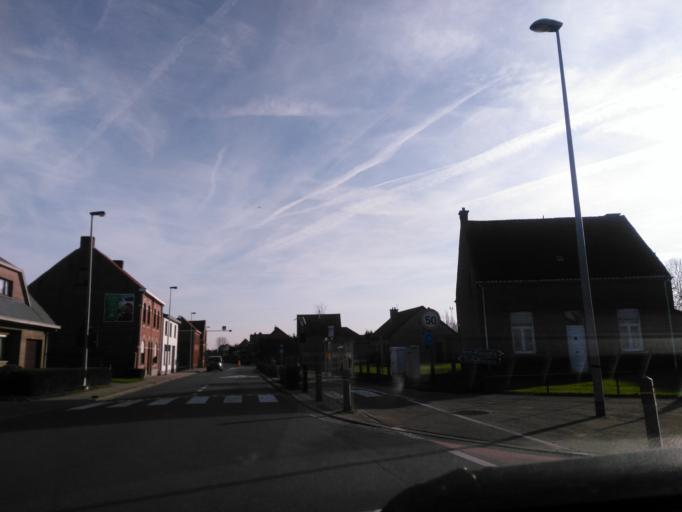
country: BE
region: Flanders
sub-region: Provincie Oost-Vlaanderen
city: Sint-Gillis-Waas
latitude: 51.2075
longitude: 4.1432
